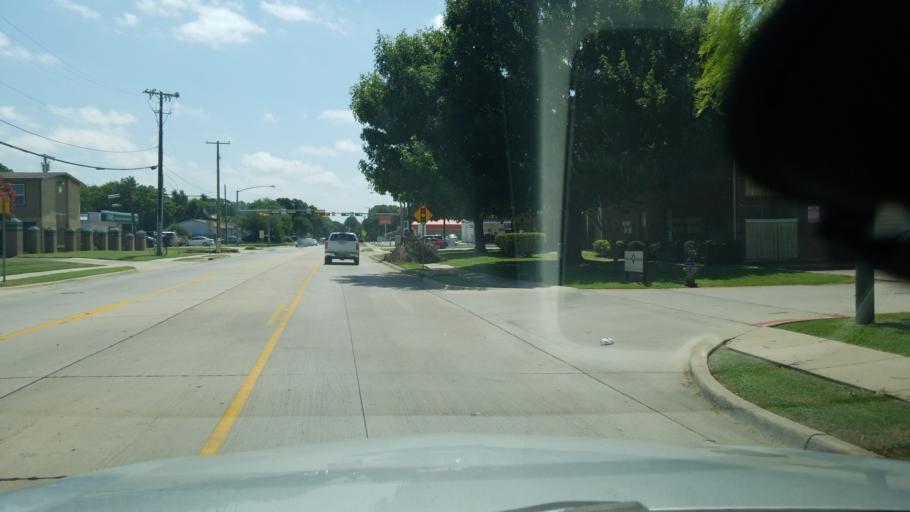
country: US
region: Texas
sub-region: Dallas County
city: Irving
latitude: 32.8296
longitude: -96.9367
